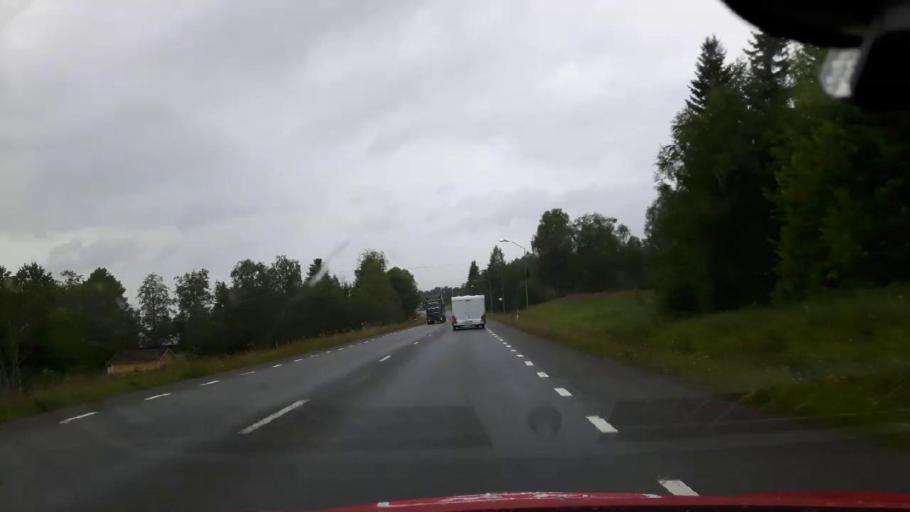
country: SE
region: Jaemtland
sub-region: Are Kommun
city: Jarpen
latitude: 63.3137
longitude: 13.5971
